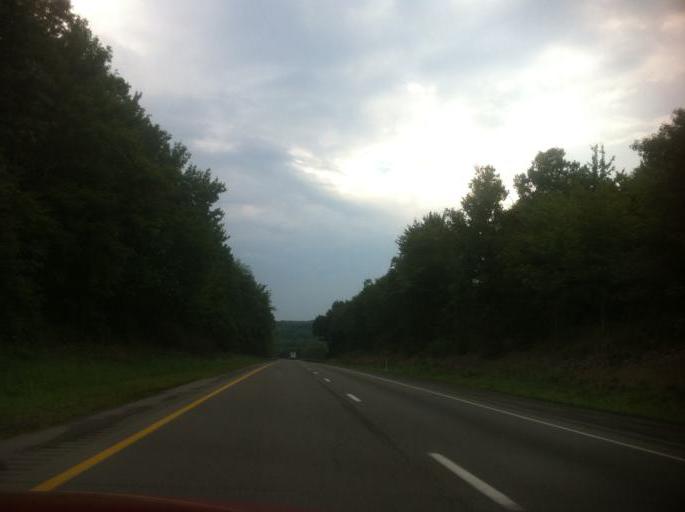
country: US
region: Pennsylvania
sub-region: Jefferson County
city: Brookville
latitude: 41.1766
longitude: -79.1176
